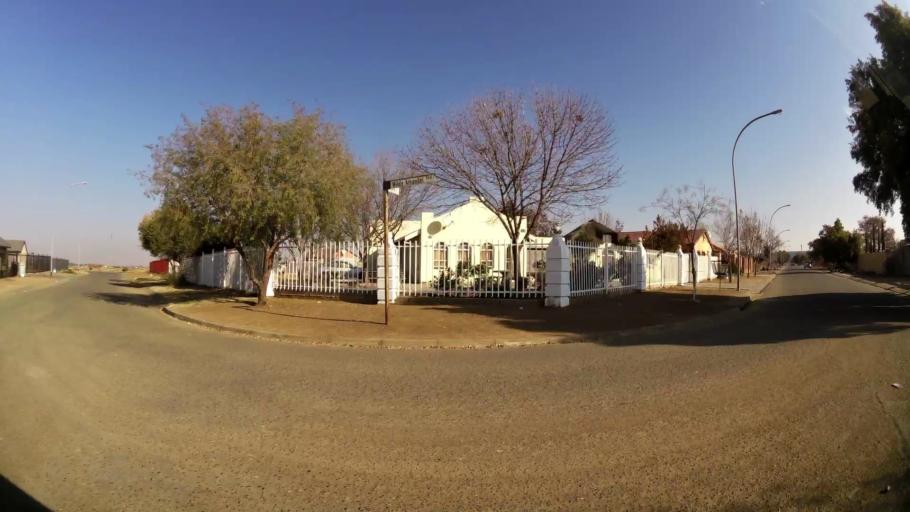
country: ZA
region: Orange Free State
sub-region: Mangaung Metropolitan Municipality
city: Bloemfontein
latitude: -29.1862
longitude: 26.1742
